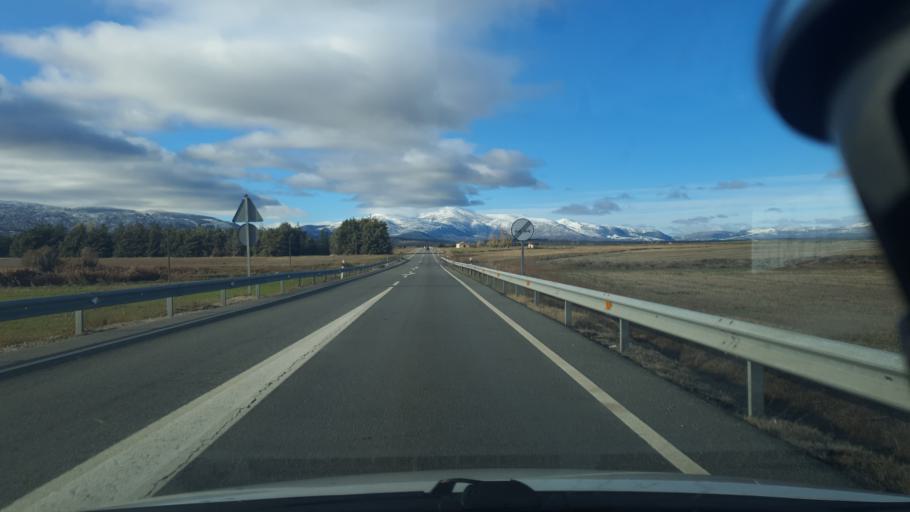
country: ES
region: Castille and Leon
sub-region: Provincia de Avila
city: Munogalindo
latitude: 40.5822
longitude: -4.8760
